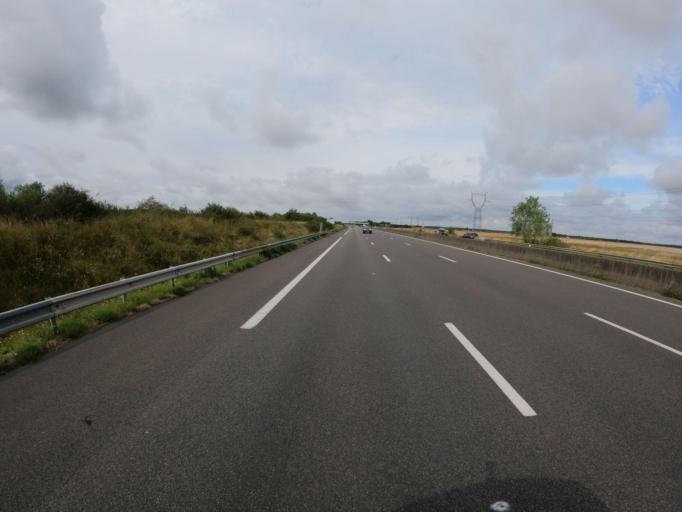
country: FR
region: Centre
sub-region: Departement du Loir-et-Cher
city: Herbault
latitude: 47.6145
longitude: 1.1549
